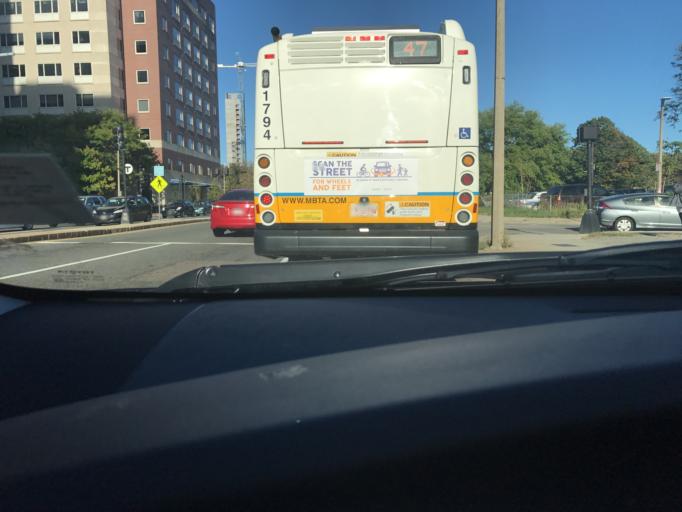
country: US
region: Massachusetts
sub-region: Norfolk County
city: Brookline
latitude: 42.3347
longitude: -71.0888
